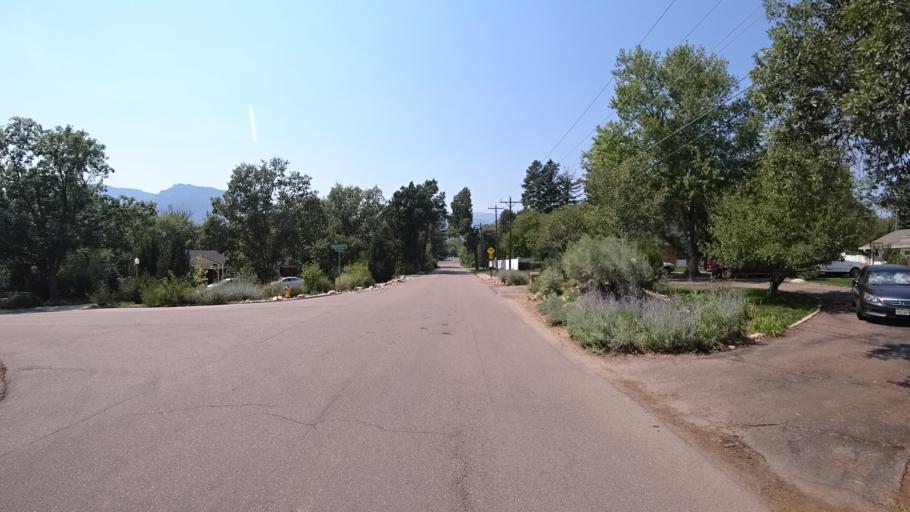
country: US
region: Colorado
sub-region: El Paso County
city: Colorado Springs
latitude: 38.7986
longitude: -104.8318
